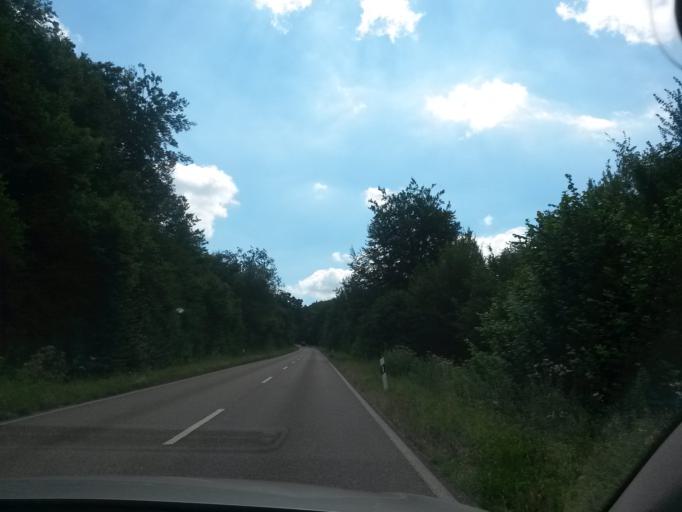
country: DE
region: Baden-Wuerttemberg
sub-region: Karlsruhe Region
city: Ettlingen
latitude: 48.9198
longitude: 8.3889
